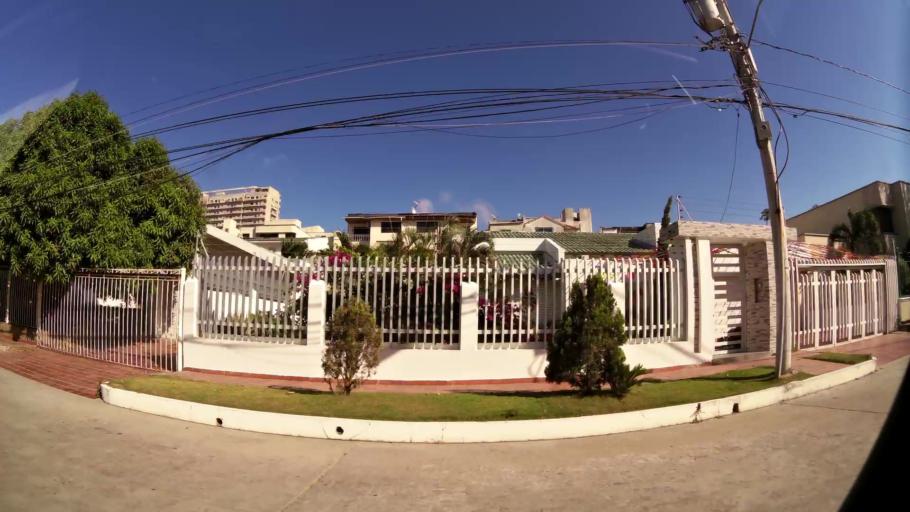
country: CO
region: Atlantico
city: Barranquilla
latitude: 11.0095
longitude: -74.8304
